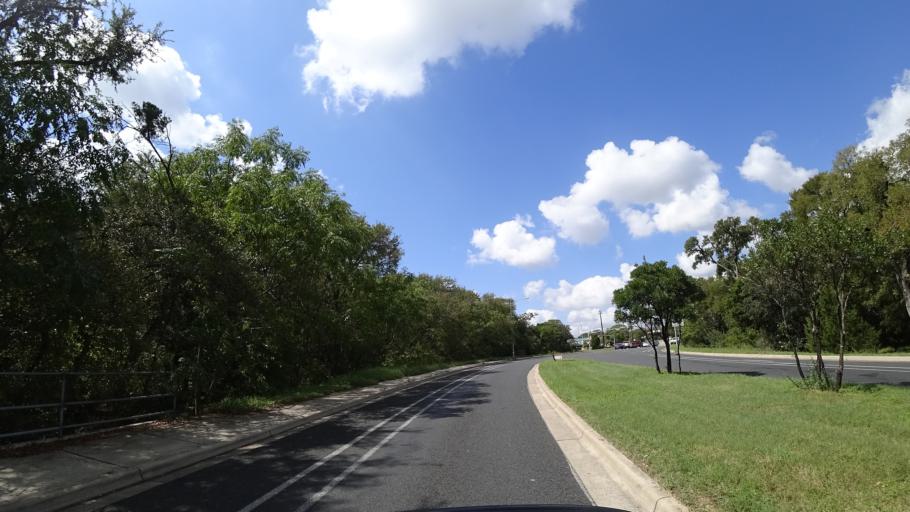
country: US
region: Texas
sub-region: Travis County
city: Manchaca
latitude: 30.1855
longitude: -97.8151
